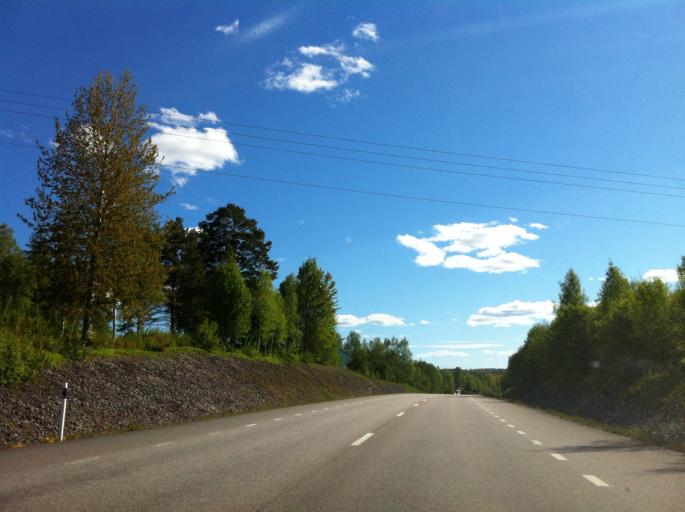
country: SE
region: Dalarna
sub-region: Rattviks Kommun
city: Raettvik
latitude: 60.8477
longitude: 15.1058
